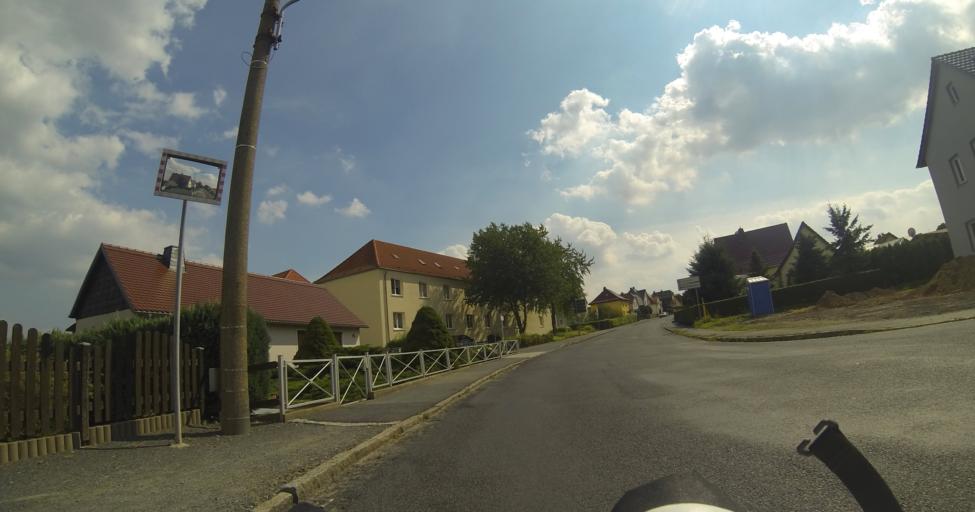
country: DE
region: Saxony
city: Grossenhain
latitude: 51.2897
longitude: 13.5434
